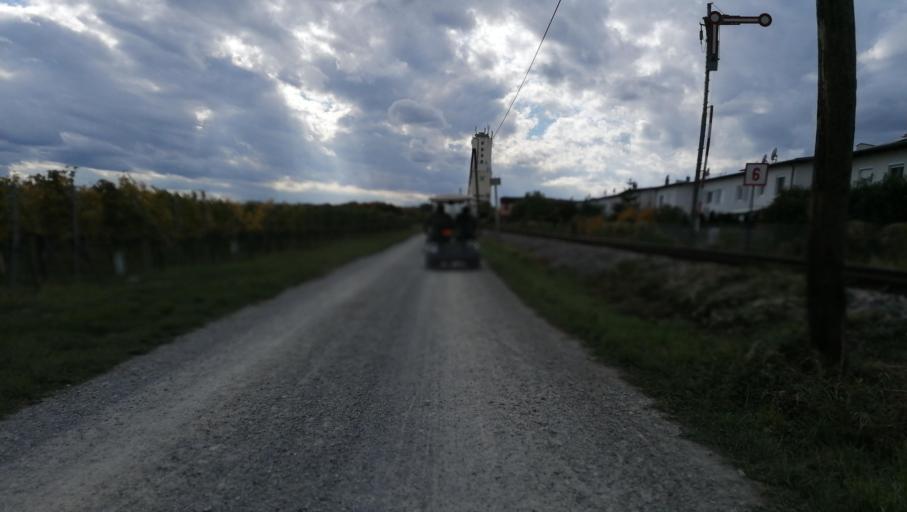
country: AT
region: Lower Austria
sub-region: Politischer Bezirk Baden
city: Tattendorf
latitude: 47.9603
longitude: 16.3119
